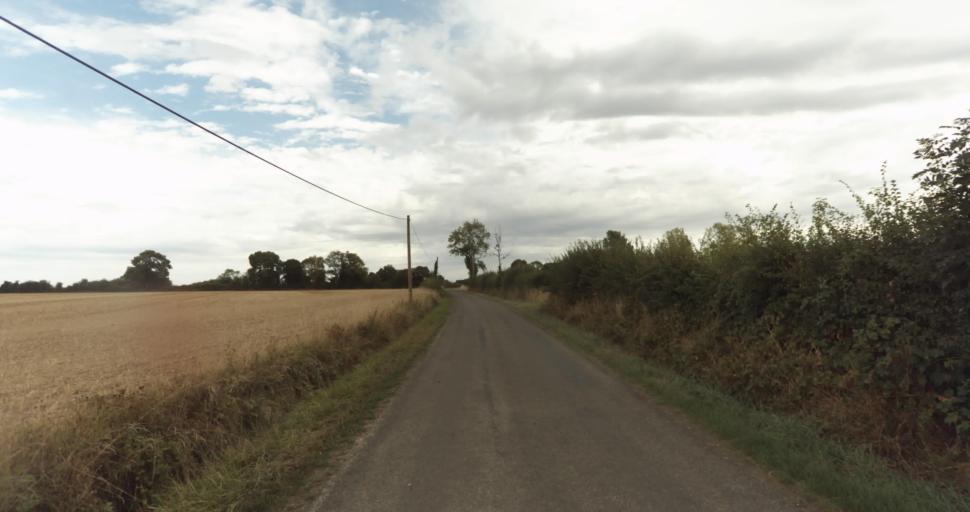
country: FR
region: Lower Normandy
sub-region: Departement du Calvados
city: La Vespiere
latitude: 48.9356
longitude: 0.3339
